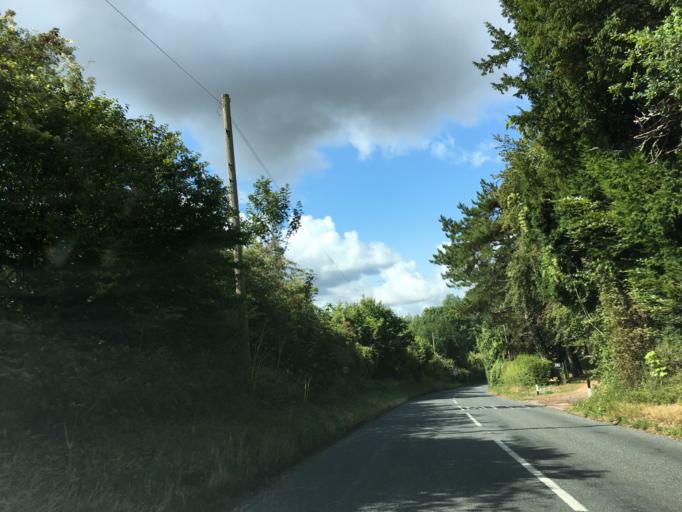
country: GB
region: England
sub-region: Hampshire
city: Overton
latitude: 51.2151
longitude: -1.3672
